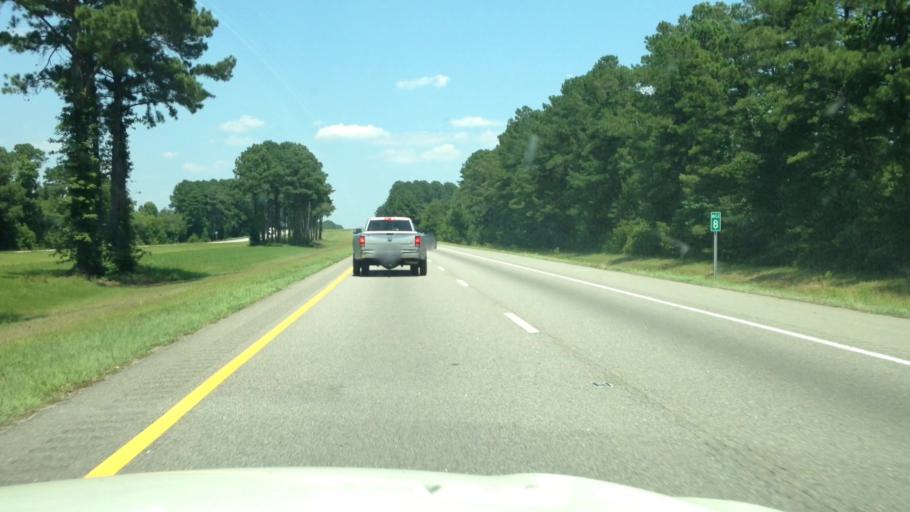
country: US
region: North Carolina
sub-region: Robeson County
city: Fairmont
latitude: 34.5568
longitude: -79.1867
